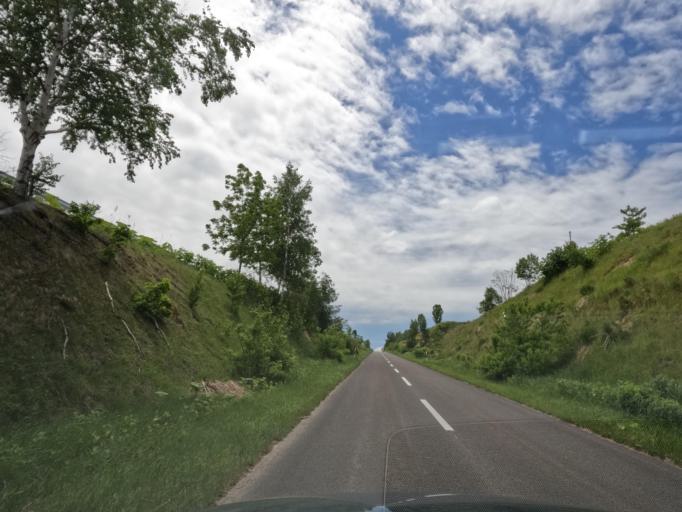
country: JP
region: Hokkaido
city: Shimo-furano
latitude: 43.5120
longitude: 142.4230
